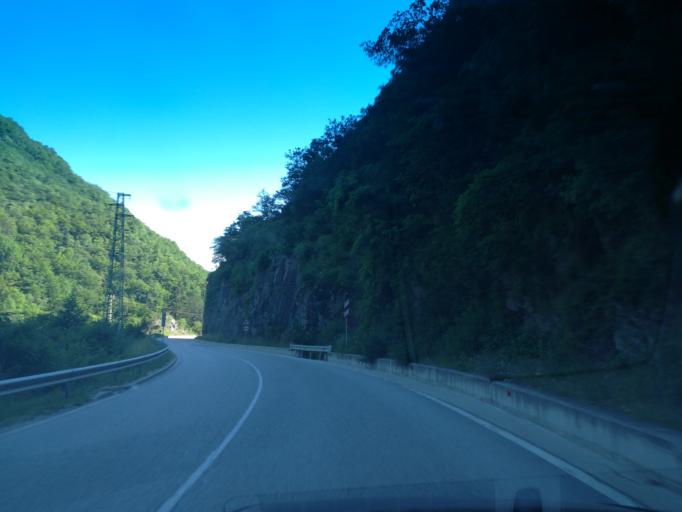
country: BG
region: Smolyan
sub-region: Obshtina Chepelare
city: Chepelare
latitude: 41.7844
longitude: 24.7079
